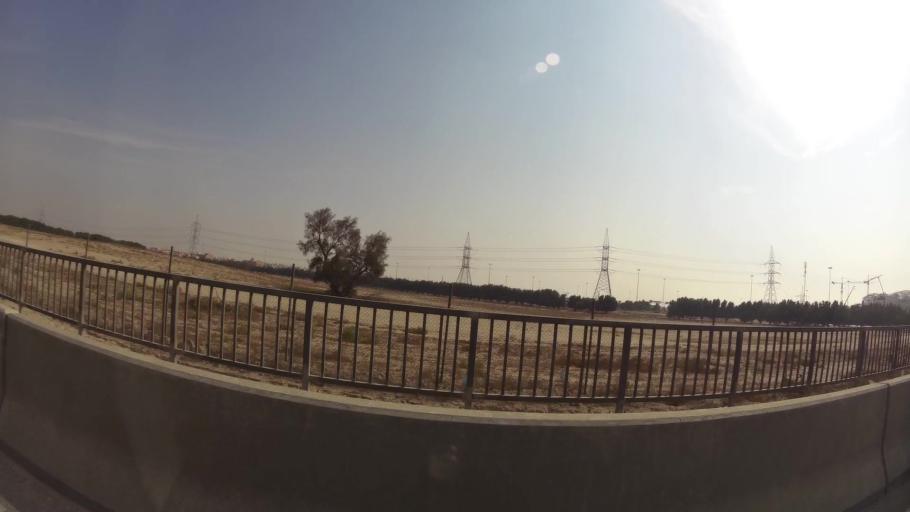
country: KW
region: Al Asimah
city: Ar Rabiyah
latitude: 29.3066
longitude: 47.9466
